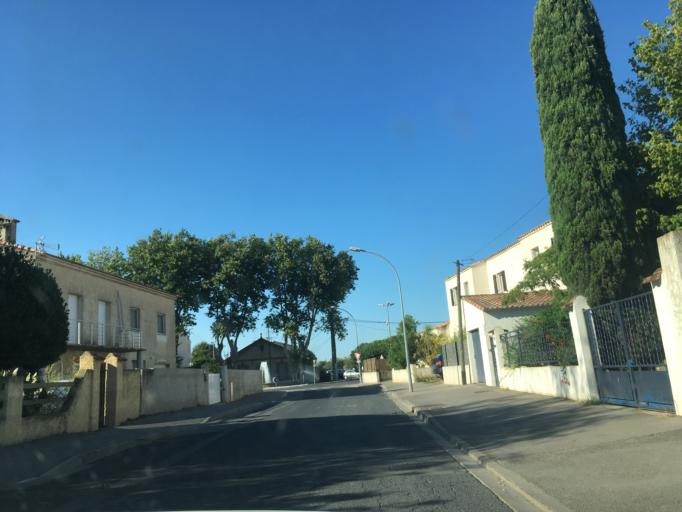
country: FR
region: Languedoc-Roussillon
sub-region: Departement du Gard
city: Aigues-Mortes
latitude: 43.5671
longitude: 4.1989
